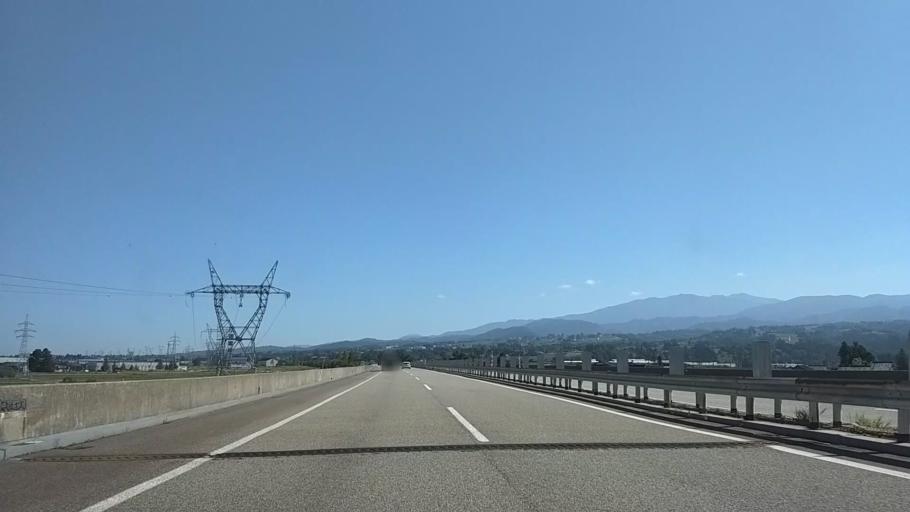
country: JP
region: Toyama
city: Kamiichi
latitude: 36.7277
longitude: 137.3619
